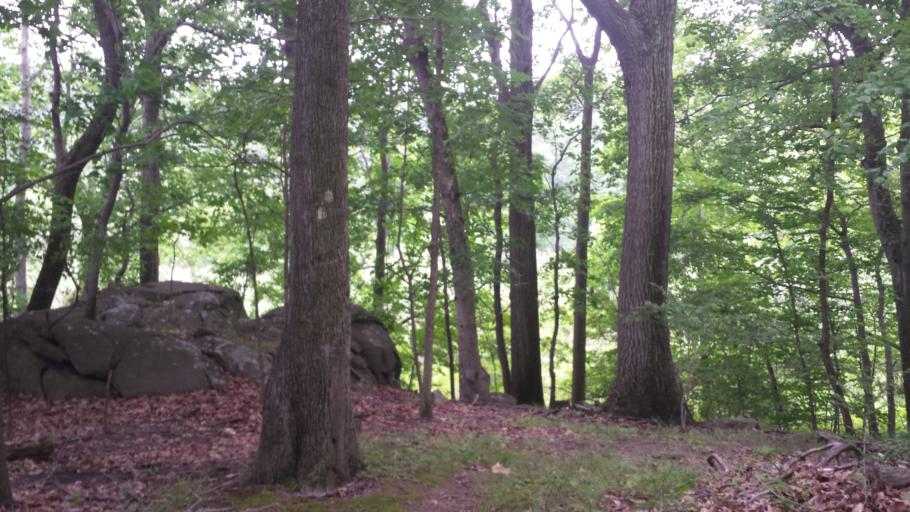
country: US
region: New York
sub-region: Westchester County
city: Montrose
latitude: 41.2403
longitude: -73.9424
